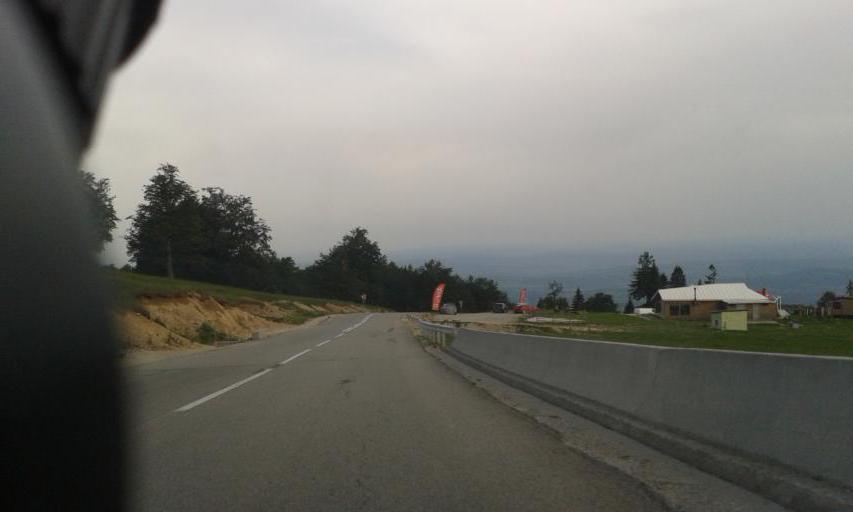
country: RO
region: Gorj
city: Novaci-Straini
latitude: 45.2408
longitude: 23.6962
